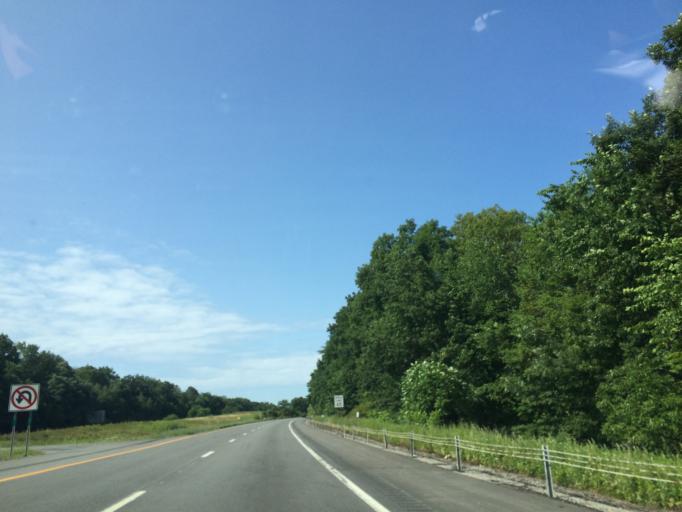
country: US
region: New York
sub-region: Orange County
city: Mechanicstown
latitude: 41.4399
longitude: -74.3779
